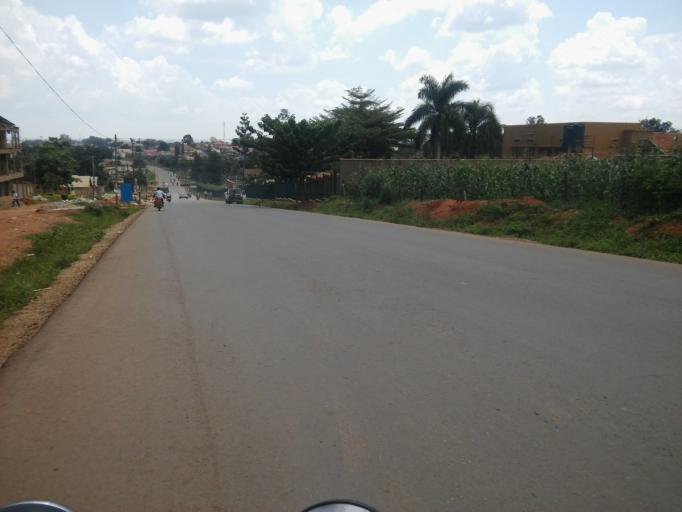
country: UG
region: Eastern Region
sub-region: Mbale District
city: Mbale
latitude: 1.0728
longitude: 34.1728
